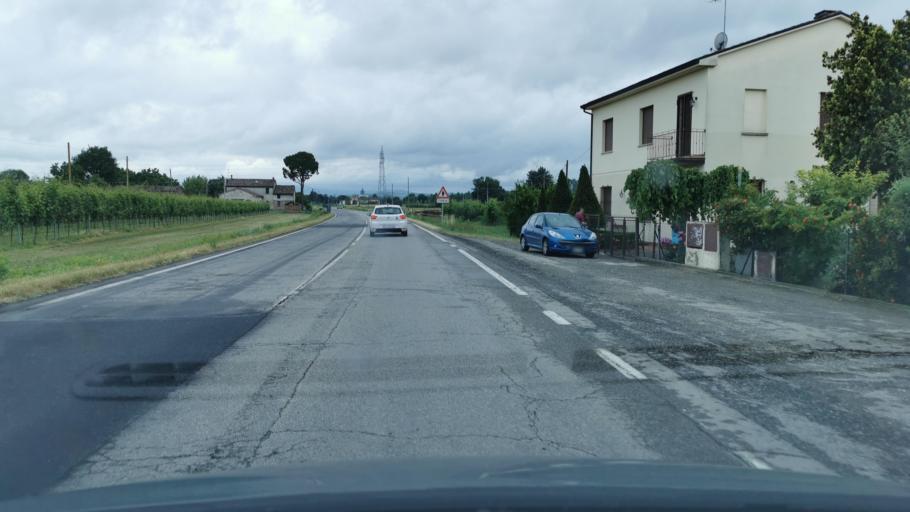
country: IT
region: Emilia-Romagna
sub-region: Provincia di Ravenna
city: Faenza
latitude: 44.3091
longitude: 11.8871
